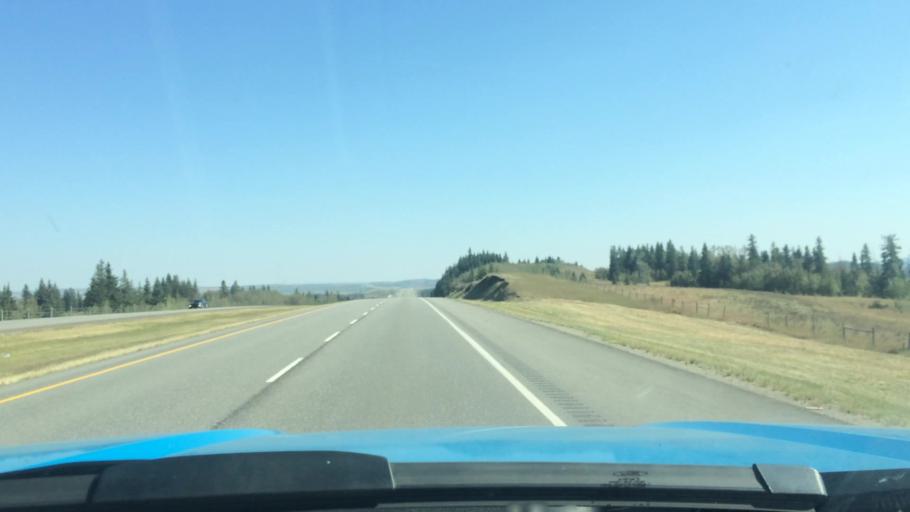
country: CA
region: Alberta
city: Cochrane
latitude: 51.1396
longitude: -114.7157
